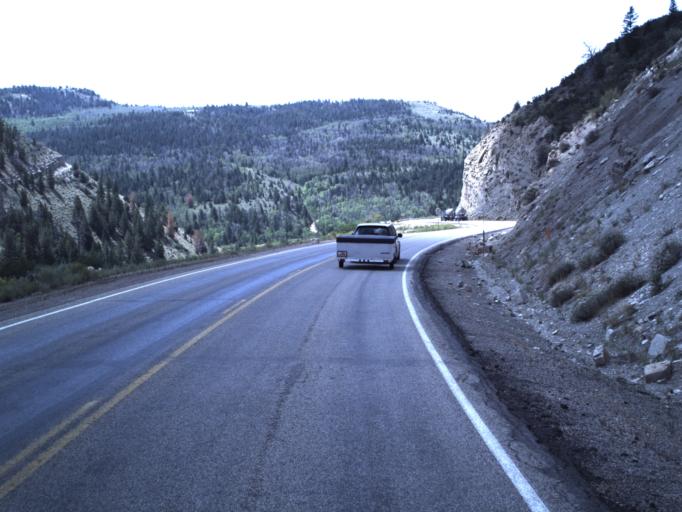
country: US
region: Utah
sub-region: Carbon County
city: Helper
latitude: 39.8534
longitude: -110.7655
